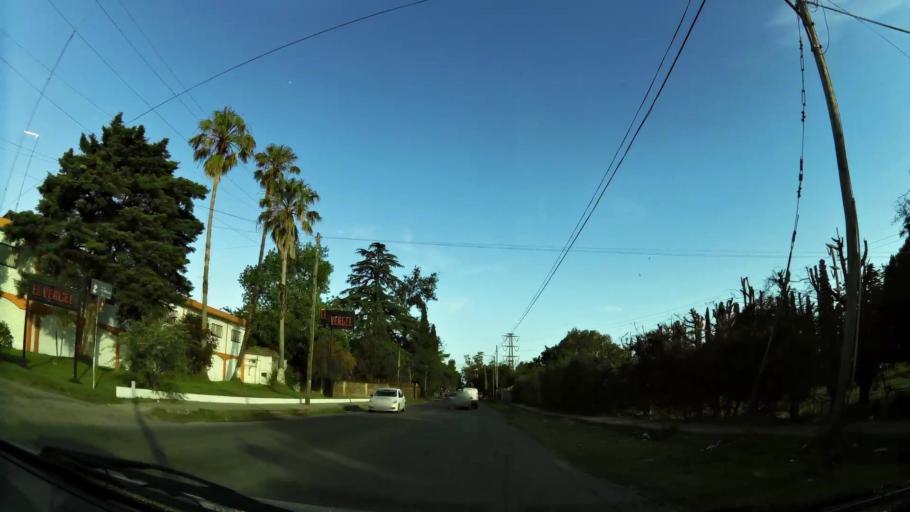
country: AR
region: Buenos Aires
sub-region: Partido de Quilmes
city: Quilmes
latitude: -34.8105
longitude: -58.2082
